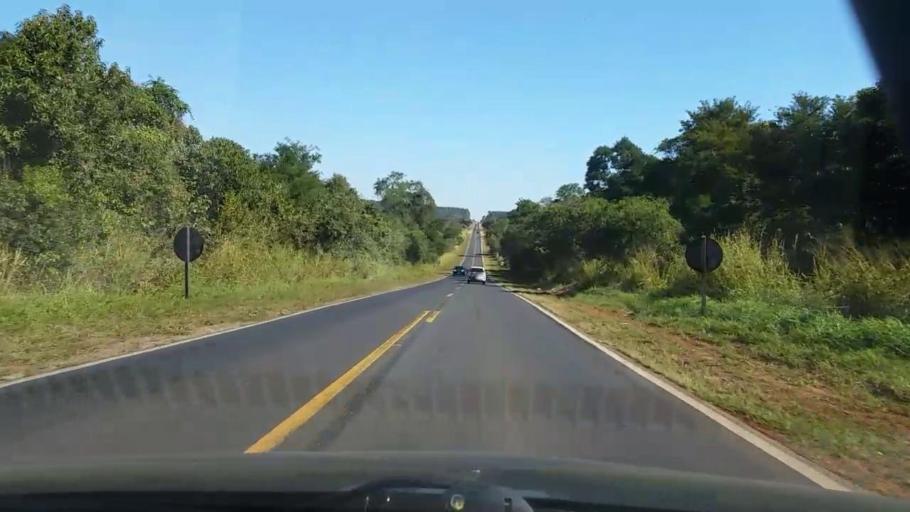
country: BR
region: Sao Paulo
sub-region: Avare
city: Avare
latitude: -22.9107
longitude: -48.7738
